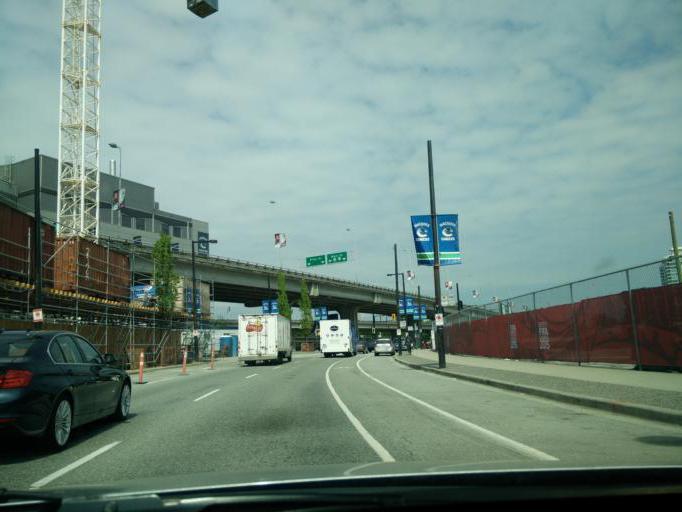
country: CA
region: British Columbia
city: West End
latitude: 49.2768
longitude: -123.1090
